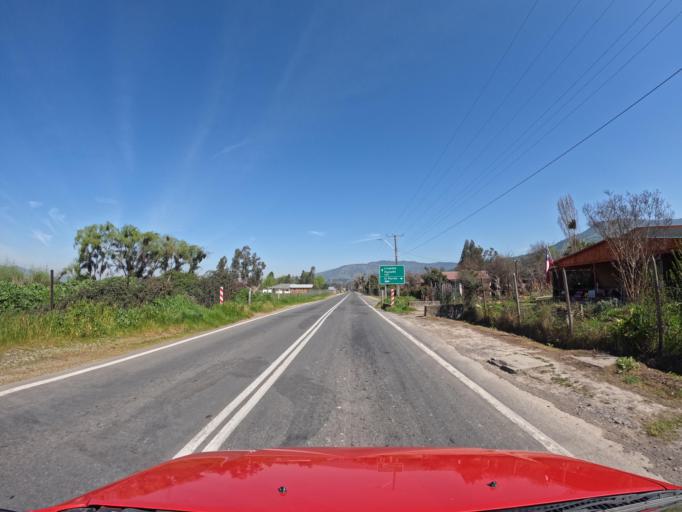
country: CL
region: Maule
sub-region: Provincia de Curico
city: Rauco
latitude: -34.9789
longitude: -71.3984
